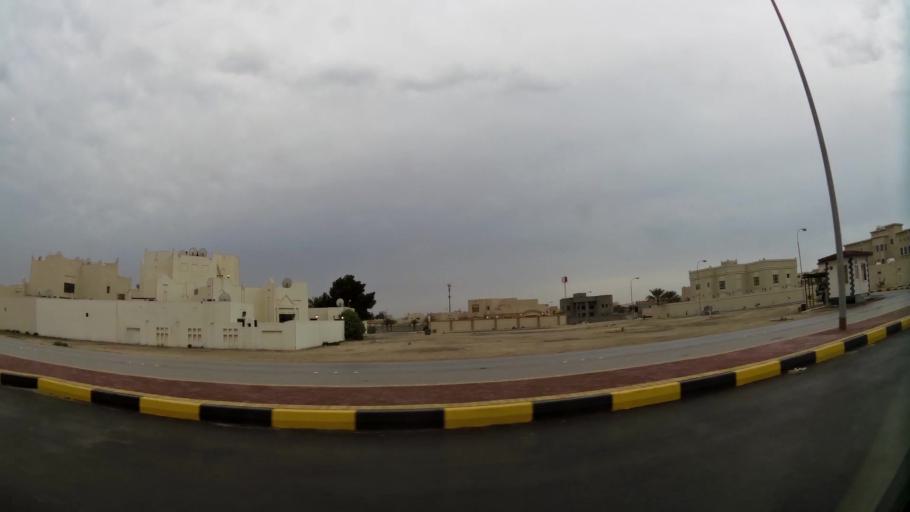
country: BH
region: Central Governorate
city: Madinat Hamad
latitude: 26.1440
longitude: 50.5171
